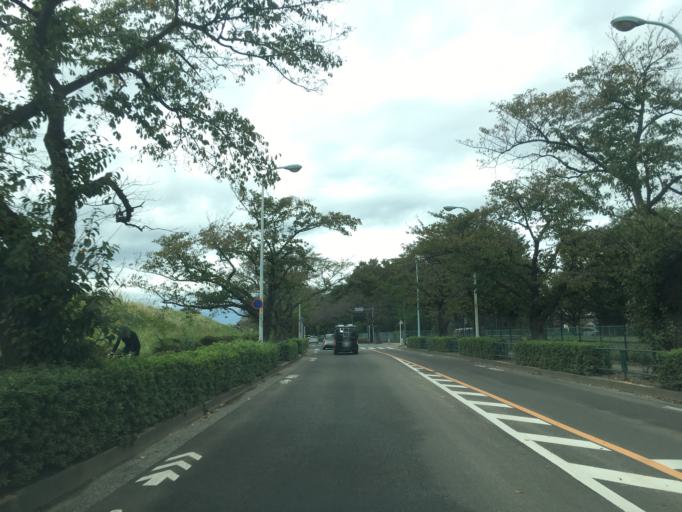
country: JP
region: Tokyo
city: Chofugaoka
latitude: 35.6351
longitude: 139.5634
